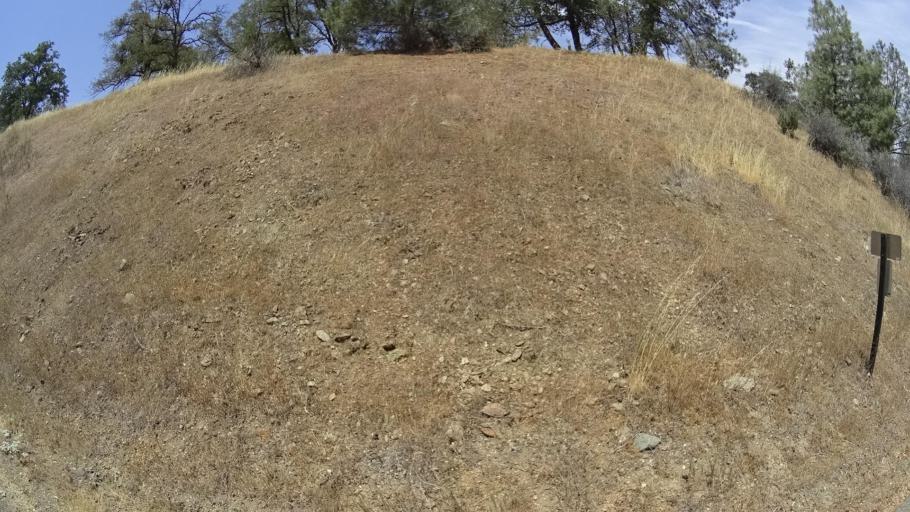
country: US
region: California
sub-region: Tuolumne County
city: Tuolumne City
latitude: 37.6453
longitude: -120.2957
